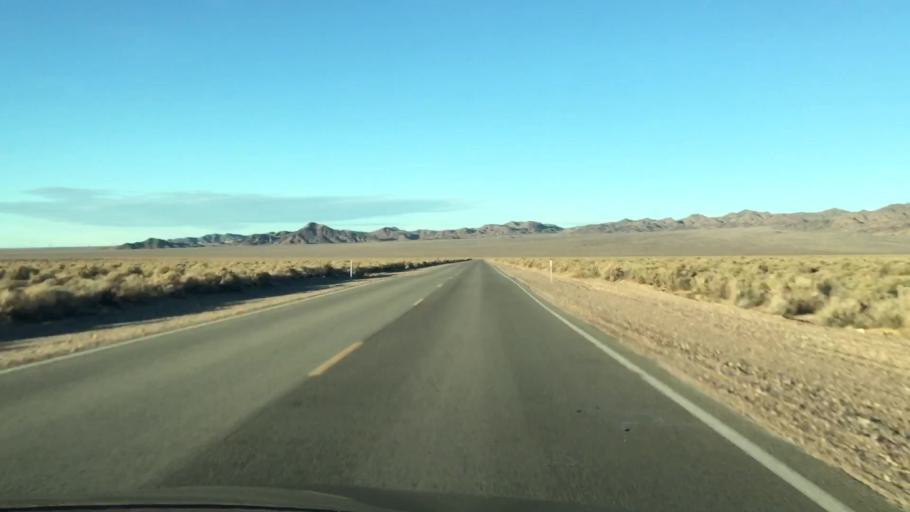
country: US
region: California
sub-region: San Bernardino County
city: Fort Irwin
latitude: 35.3178
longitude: -116.0831
